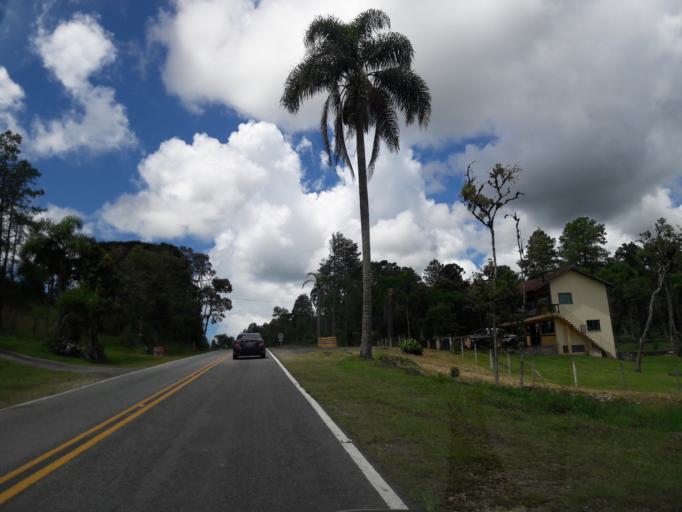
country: BR
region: Parana
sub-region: Campina Grande Do Sul
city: Campina Grande do Sul
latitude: -25.3076
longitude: -48.9434
